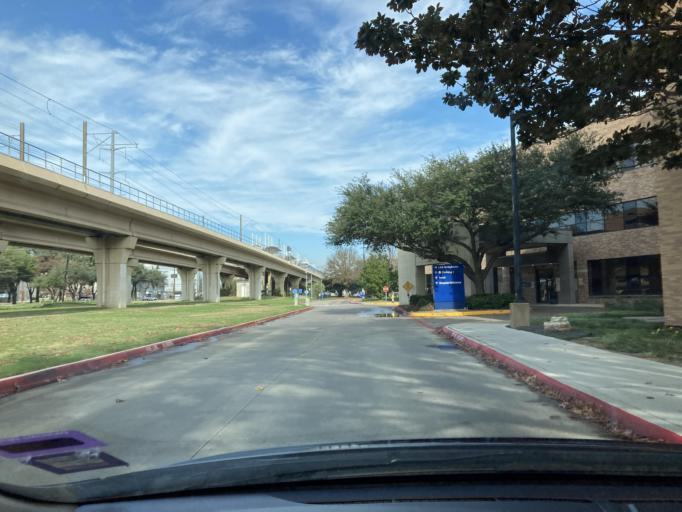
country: US
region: Texas
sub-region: Dallas County
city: University Park
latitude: 32.8808
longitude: -96.7647
